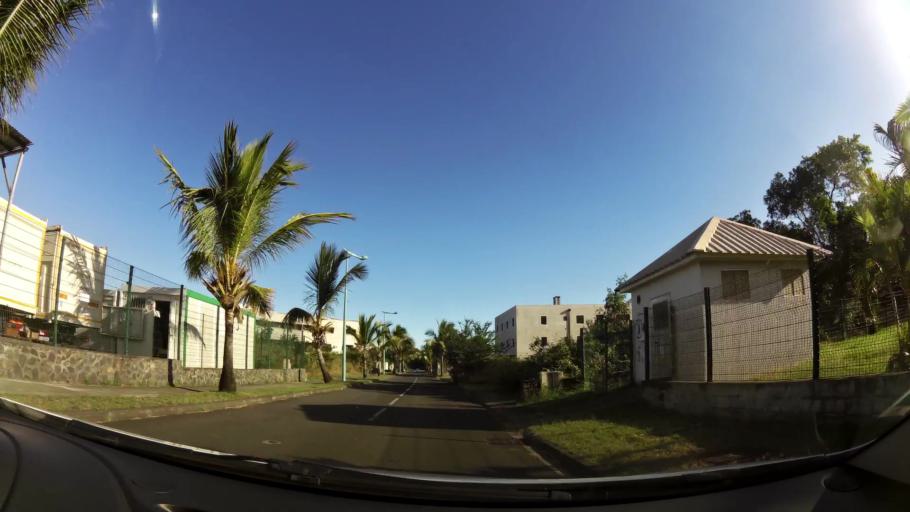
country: RE
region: Reunion
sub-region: Reunion
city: Saint-Louis
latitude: -21.2774
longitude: 55.3771
